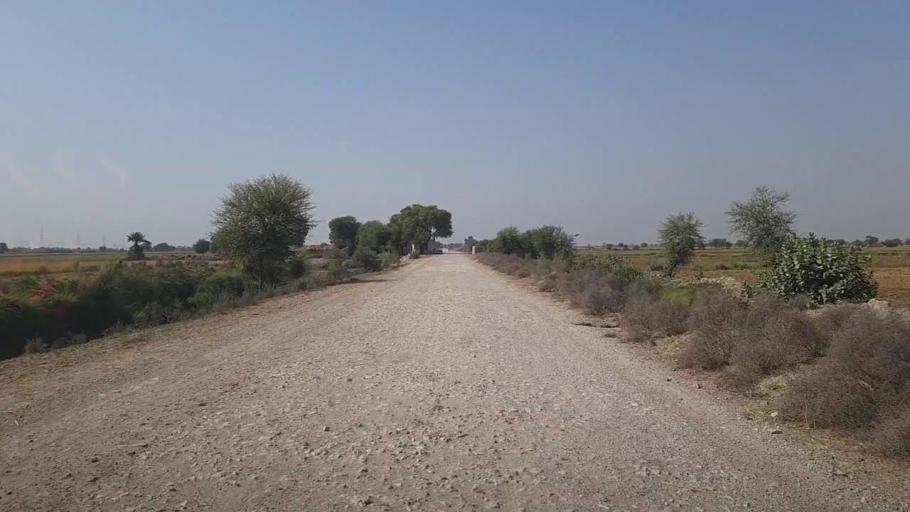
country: PK
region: Sindh
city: Kandhkot
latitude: 28.3905
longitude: 69.2869
